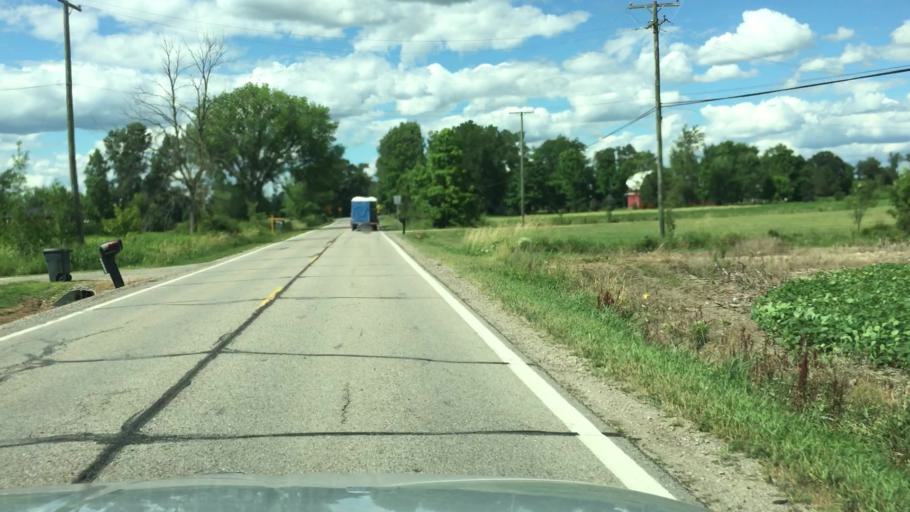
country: US
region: Michigan
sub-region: Macomb County
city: Armada
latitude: 42.8906
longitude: -82.9458
